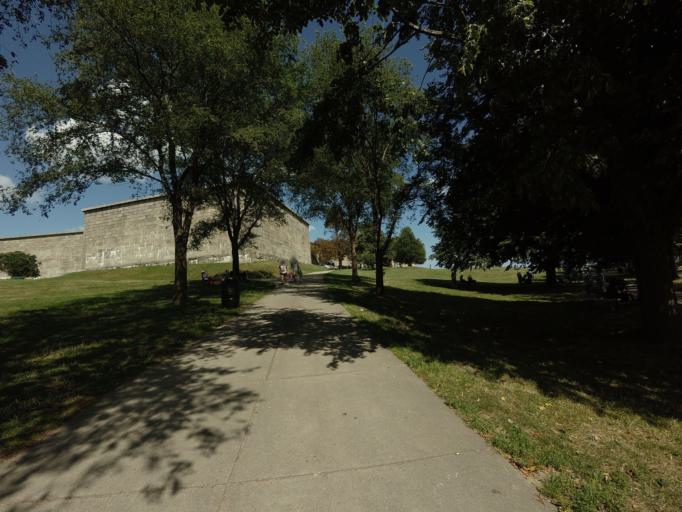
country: US
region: Massachusetts
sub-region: Suffolk County
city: South Boston
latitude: 42.3376
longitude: -71.0122
